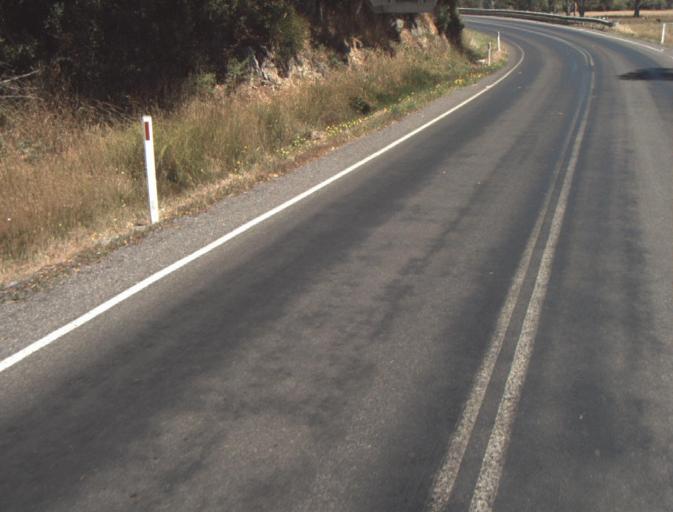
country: AU
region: Tasmania
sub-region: Launceston
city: Newstead
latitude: -41.3279
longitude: 147.3555
